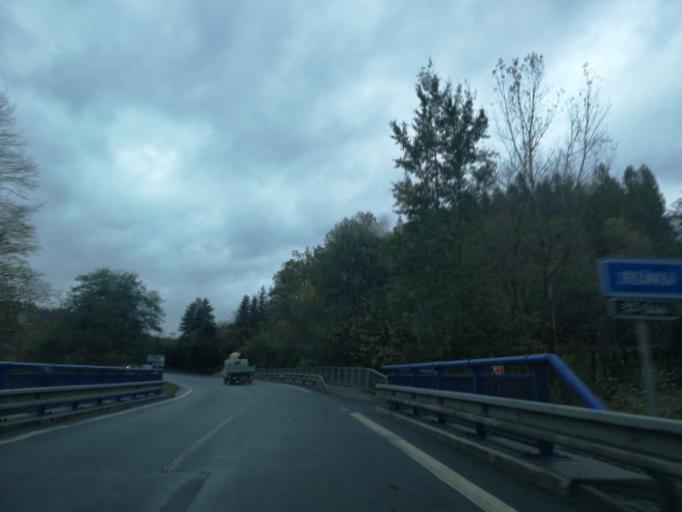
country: CZ
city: Hodslavice
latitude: 49.5282
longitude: 18.0178
